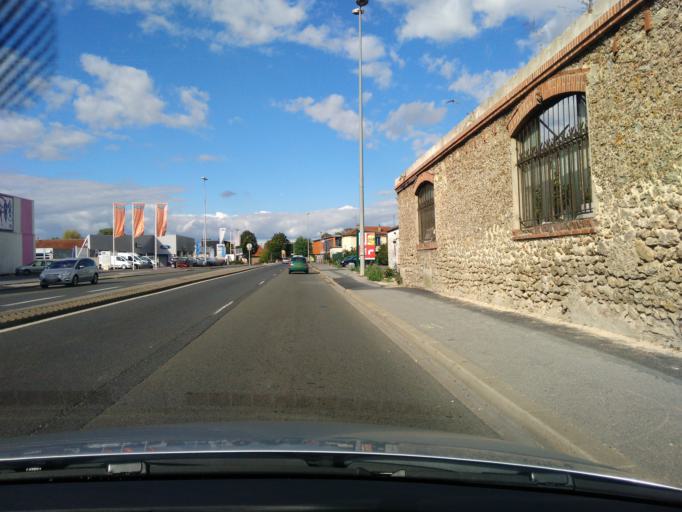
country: FR
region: Ile-de-France
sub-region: Departement de Seine-et-Marne
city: Meaux
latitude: 48.9469
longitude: 2.8798
